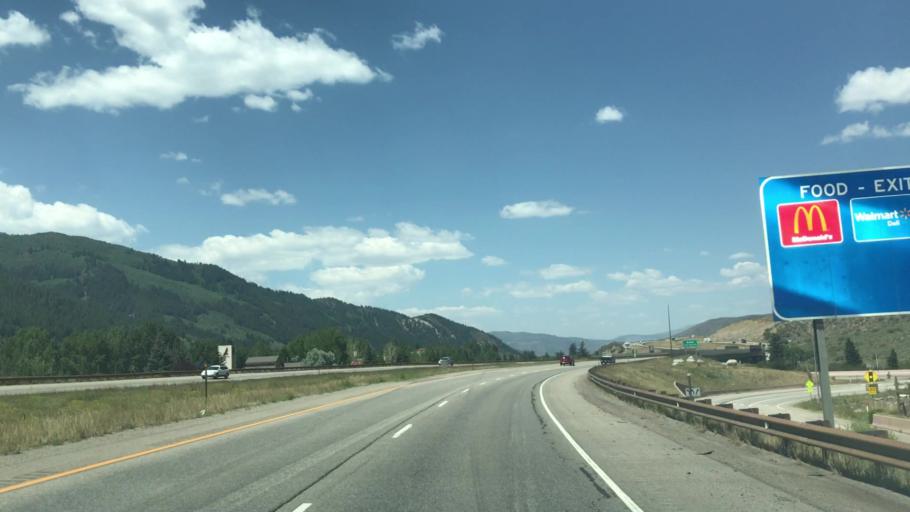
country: US
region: Colorado
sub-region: Eagle County
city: Avon
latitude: 39.6216
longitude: -106.4809
